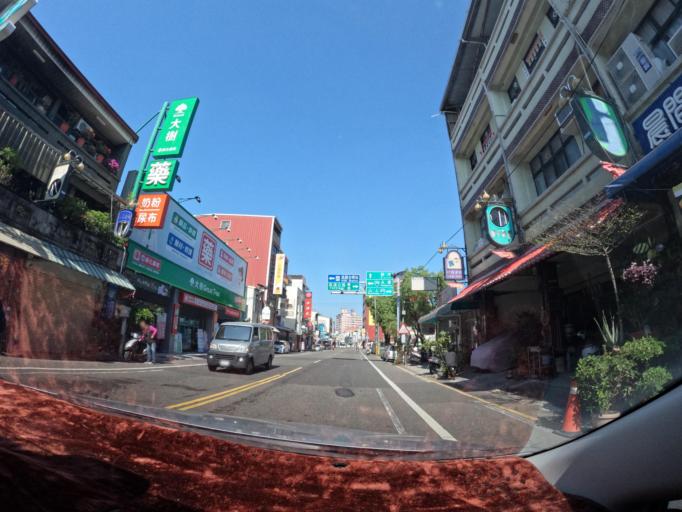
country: TW
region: Taiwan
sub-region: Tainan
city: Tainan
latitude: 23.0378
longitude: 120.3075
